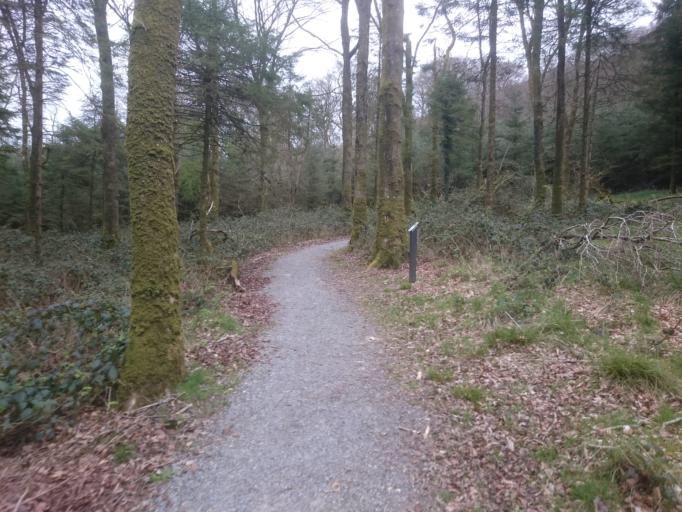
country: IE
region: Leinster
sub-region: Kilkenny
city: Callan
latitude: 52.6633
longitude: -7.5354
